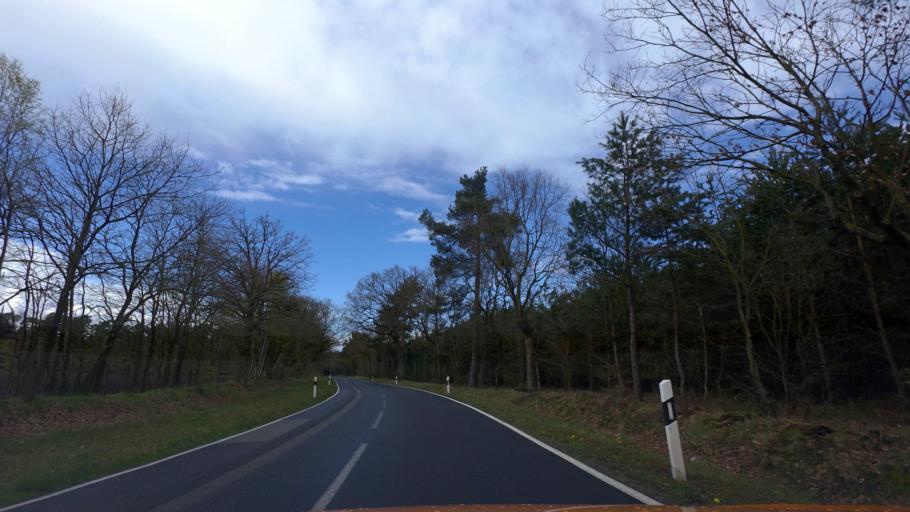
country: DE
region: Mecklenburg-Vorpommern
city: Nostorf
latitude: 53.4136
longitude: 10.6852
